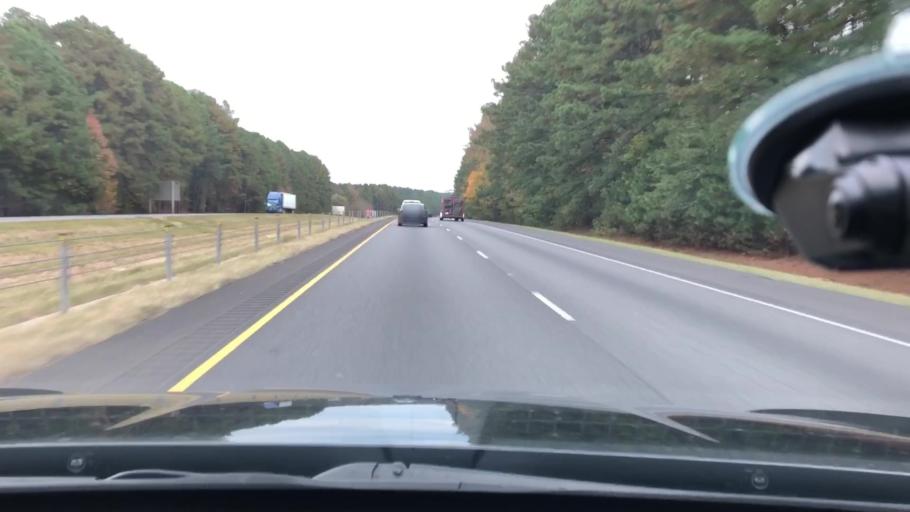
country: US
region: Arkansas
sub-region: Clark County
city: Arkadelphia
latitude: 34.2021
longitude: -93.0483
